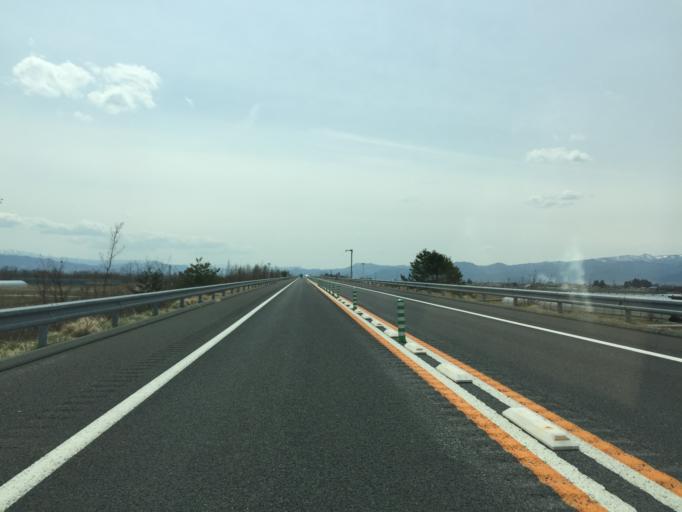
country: JP
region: Yamagata
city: Tendo
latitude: 38.3318
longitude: 140.3296
